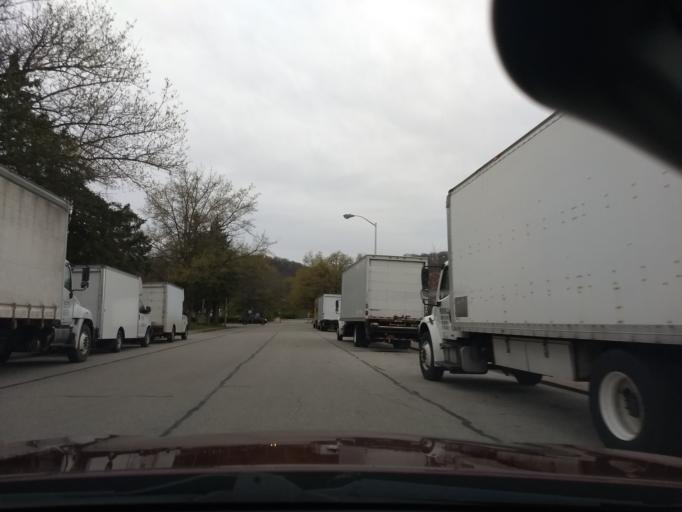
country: US
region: Pennsylvania
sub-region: Allegheny County
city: Ingram
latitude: 40.4435
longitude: -80.0815
